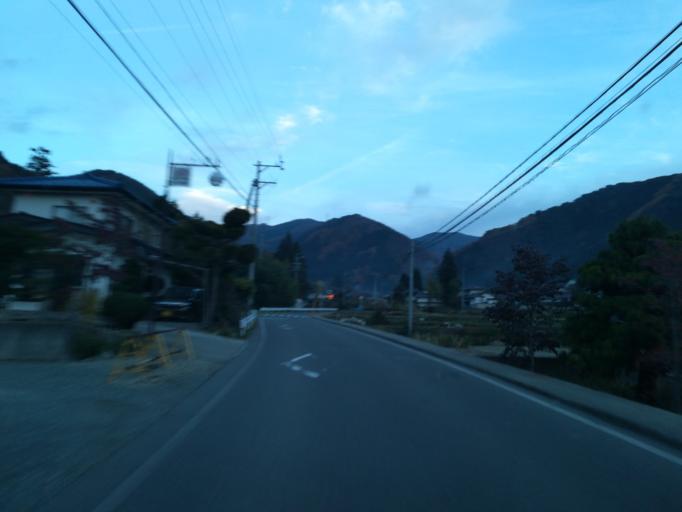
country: JP
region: Nagano
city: Suzaka
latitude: 36.5864
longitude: 138.2686
